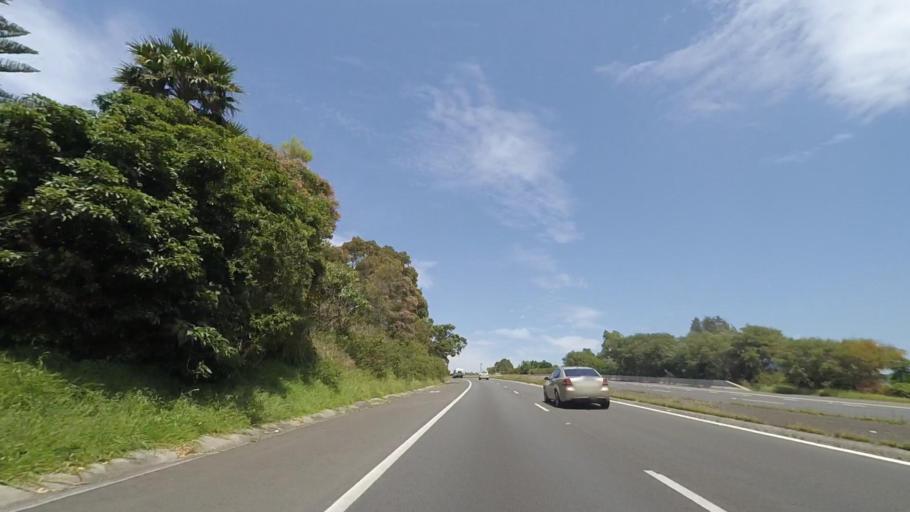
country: AU
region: New South Wales
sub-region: Kiama
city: Kiama
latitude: -34.6713
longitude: 150.8434
